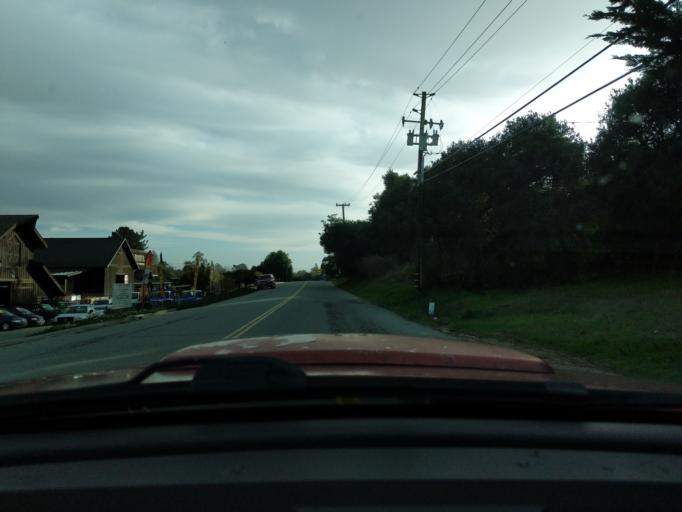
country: US
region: California
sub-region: Monterey County
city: Prunedale
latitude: 36.7950
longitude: -121.6675
